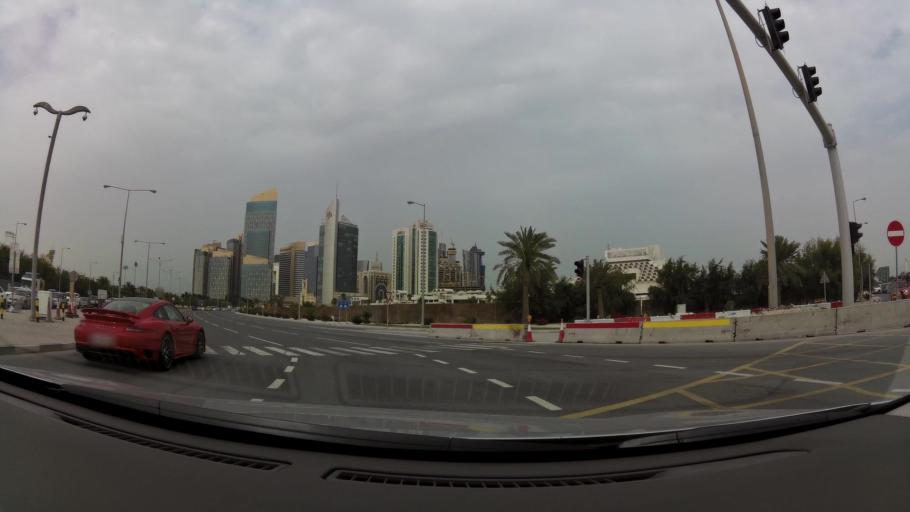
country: QA
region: Baladiyat ad Dawhah
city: Doha
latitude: 25.3099
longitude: 51.5149
